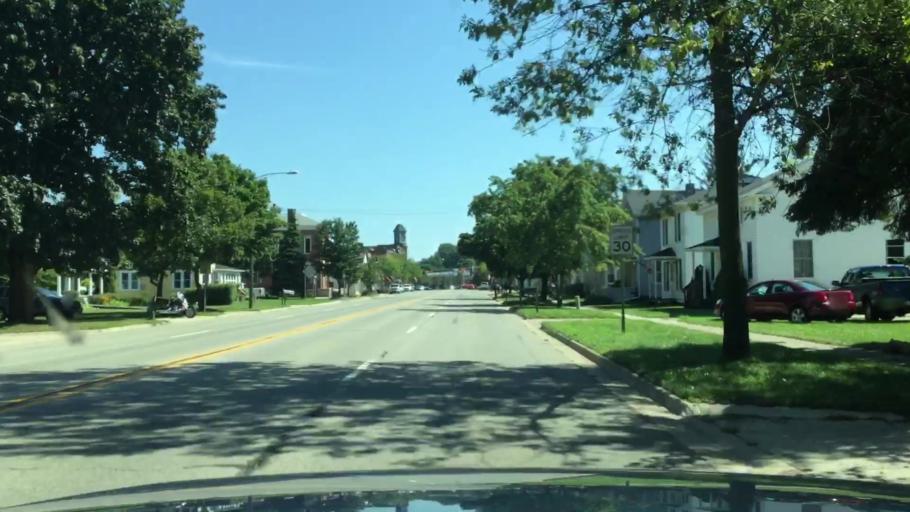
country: US
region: Michigan
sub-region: Lenawee County
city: Clinton
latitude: 42.0719
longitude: -83.9756
